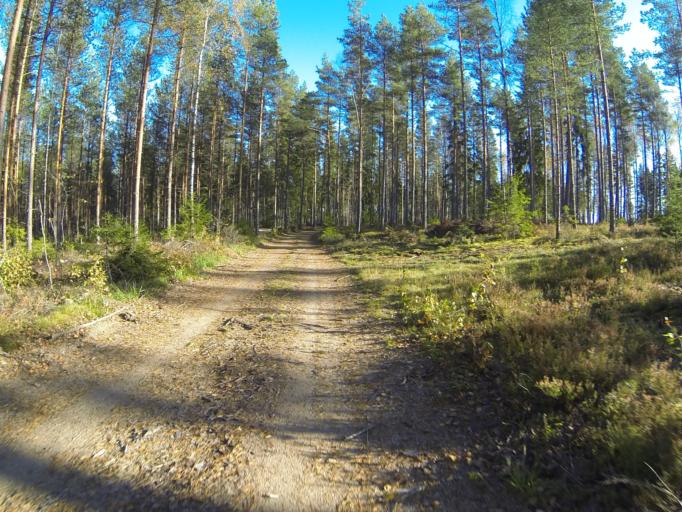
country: FI
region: Varsinais-Suomi
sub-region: Salo
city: Saerkisalo
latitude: 60.2143
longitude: 22.9818
